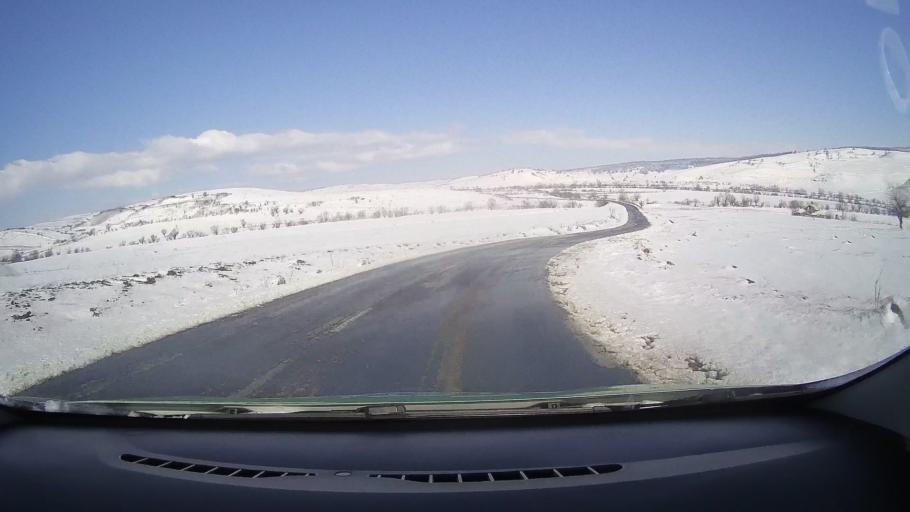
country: RO
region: Sibiu
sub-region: Comuna Rosia
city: Rosia
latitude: 45.8225
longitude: 24.3128
